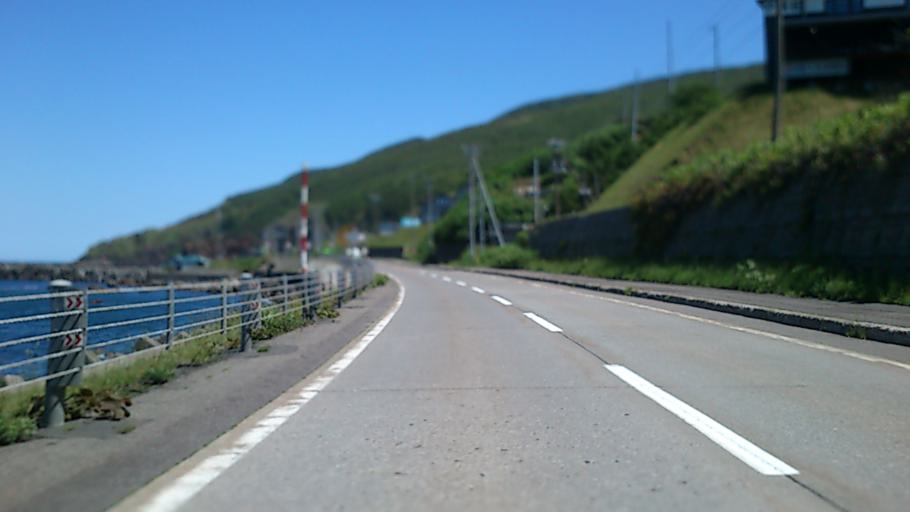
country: JP
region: Hokkaido
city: Rumoi
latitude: 43.7725
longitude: 141.3674
